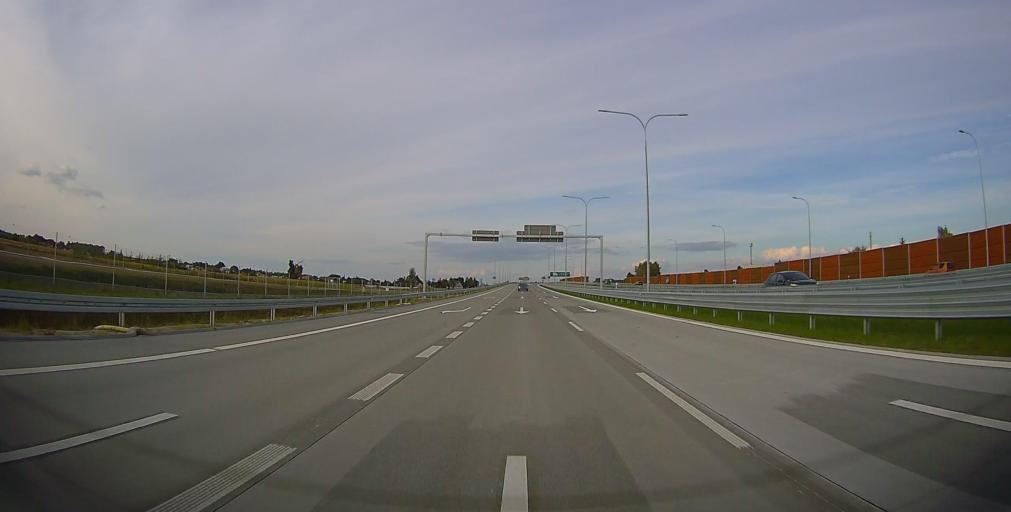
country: PL
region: Masovian Voivodeship
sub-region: Powiat piaseczynski
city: Mysiadlo
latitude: 52.1240
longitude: 20.9880
